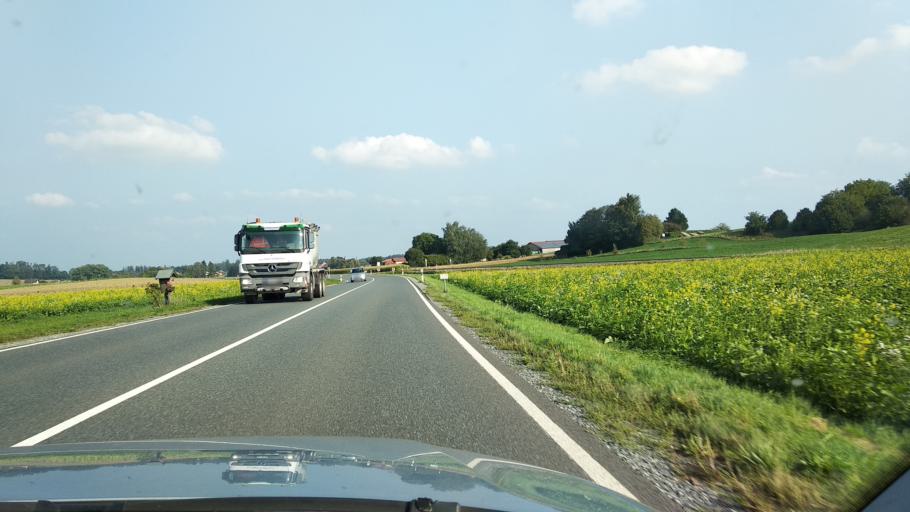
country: DE
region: Bavaria
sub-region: Upper Bavaria
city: Steinhoring
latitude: 48.0846
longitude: 12.0732
